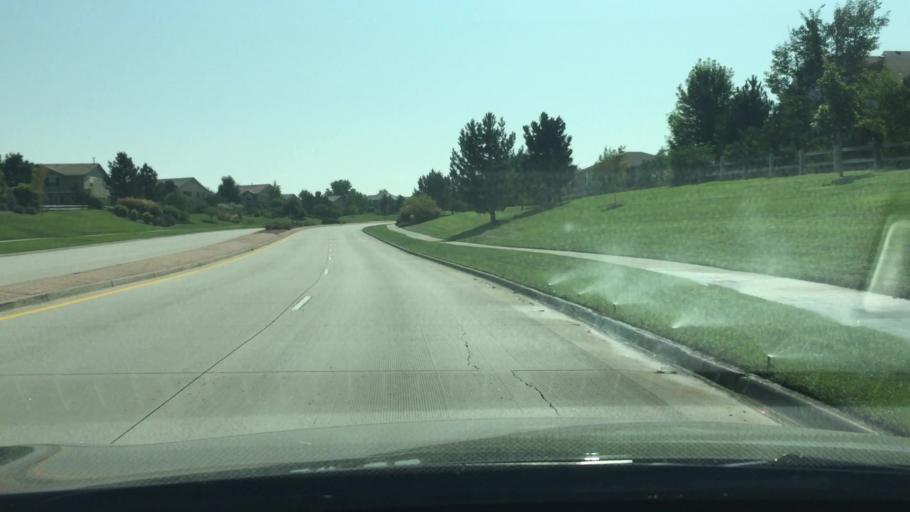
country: US
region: Colorado
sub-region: Arapahoe County
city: Dove Valley
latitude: 39.6071
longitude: -104.7902
